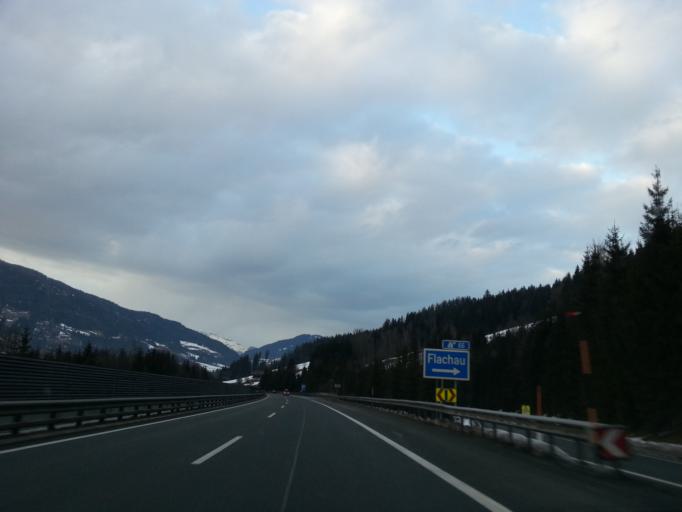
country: AT
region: Salzburg
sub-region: Politischer Bezirk Sankt Johann im Pongau
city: Flachau
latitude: 47.3582
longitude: 13.3979
